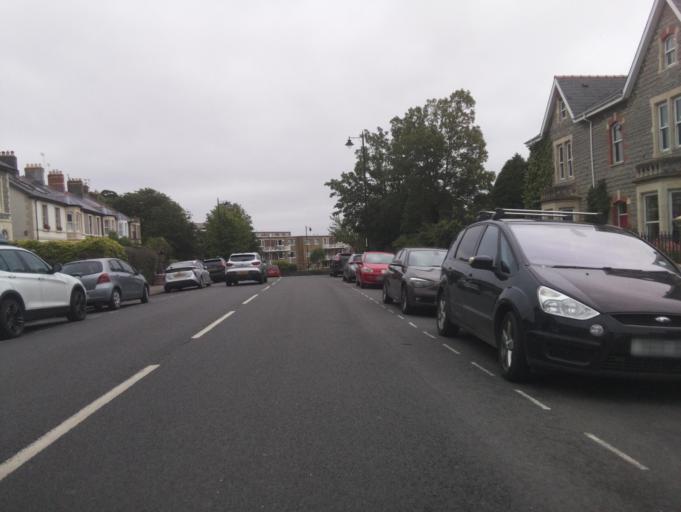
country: GB
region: Wales
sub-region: Vale of Glamorgan
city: Penarth
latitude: 51.4384
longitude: -3.1725
